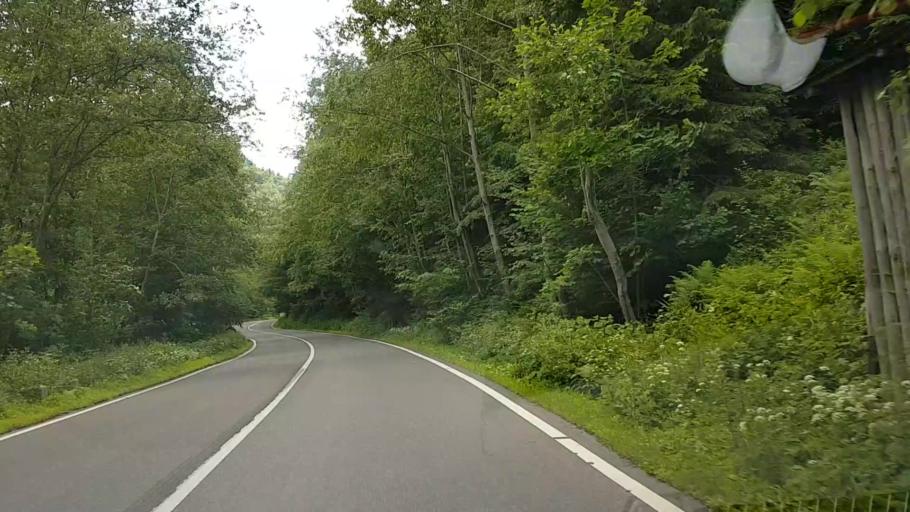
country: RO
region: Suceava
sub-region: Comuna Crucea
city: Crucea
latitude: 47.3257
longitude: 25.6220
